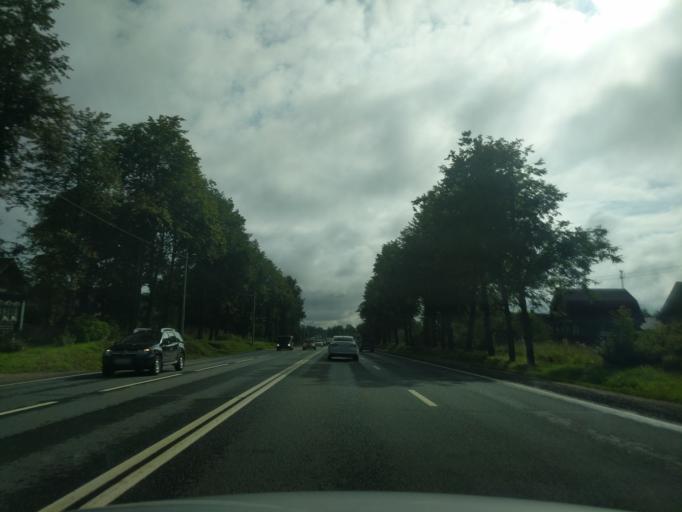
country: RU
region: Jaroslavl
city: Pereslavl'-Zalesskiy
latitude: 56.8692
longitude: 39.0533
